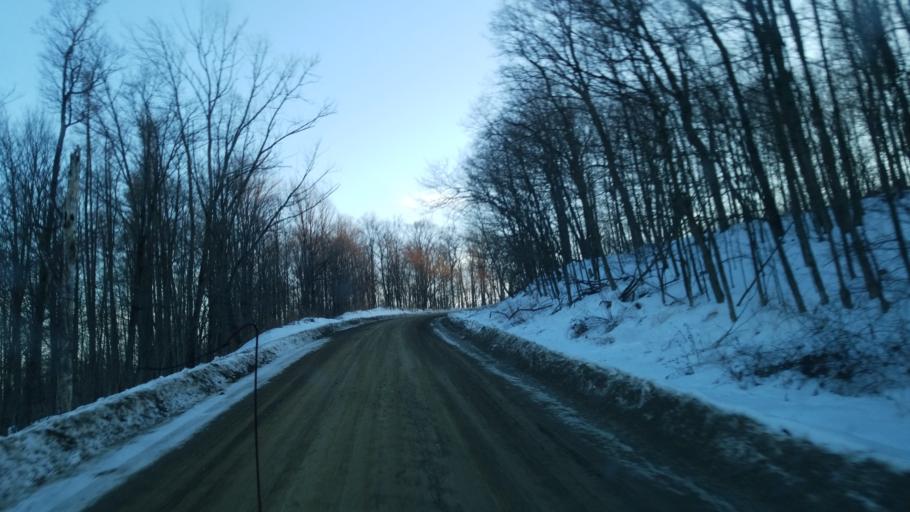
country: US
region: Pennsylvania
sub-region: Tioga County
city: Westfield
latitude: 42.0140
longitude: -77.6570
